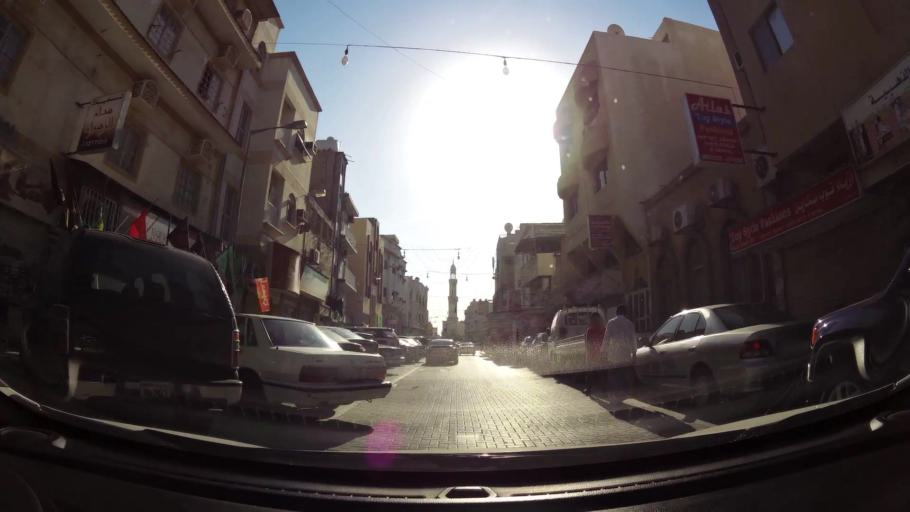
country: BH
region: Manama
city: Manama
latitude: 26.2302
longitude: 50.5773
